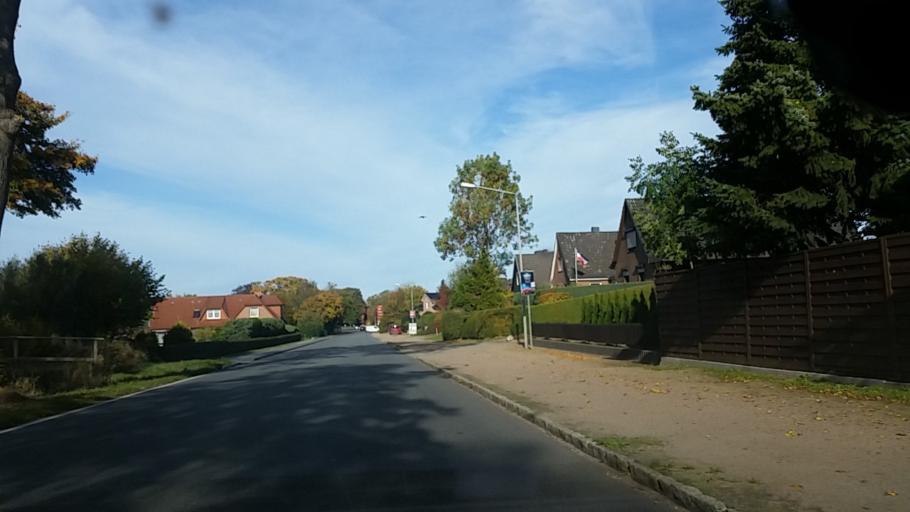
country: DE
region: Schleswig-Holstein
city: Delingsdorf
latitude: 53.7032
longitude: 10.2498
